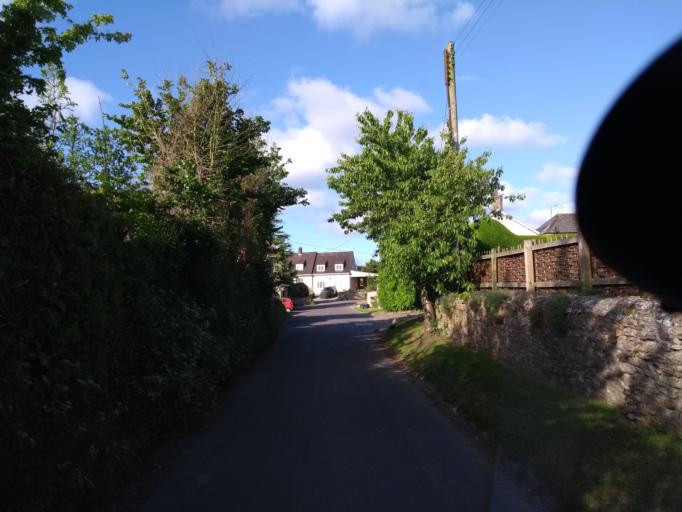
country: GB
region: England
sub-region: Somerset
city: Taunton
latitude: 50.9680
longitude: -3.1105
